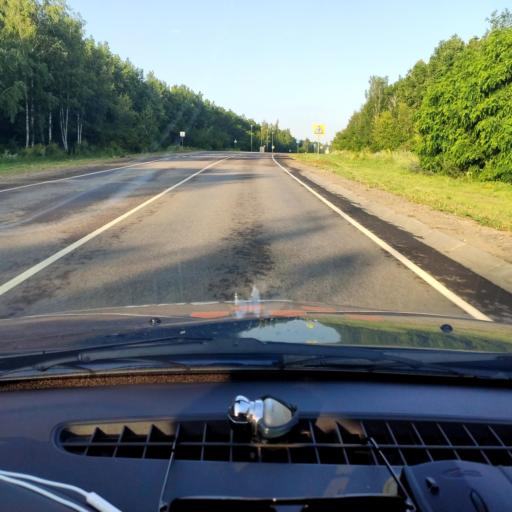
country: RU
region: Lipetsk
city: Izmalkovo
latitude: 52.4552
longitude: 38.0057
